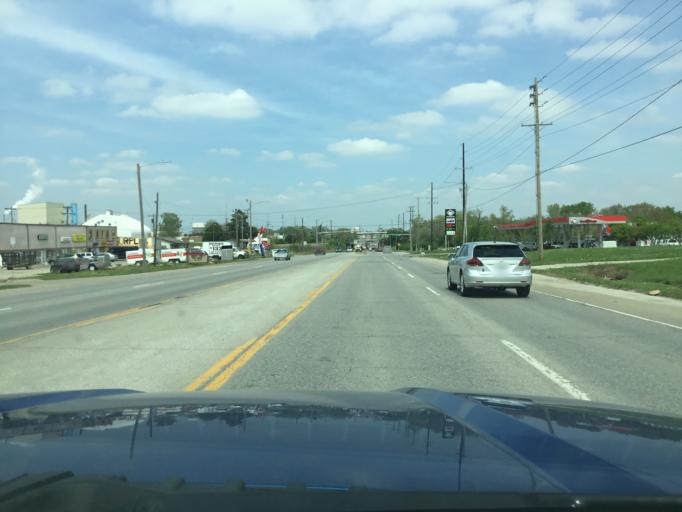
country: US
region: Kansas
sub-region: Shawnee County
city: Topeka
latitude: 38.9835
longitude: -95.6877
